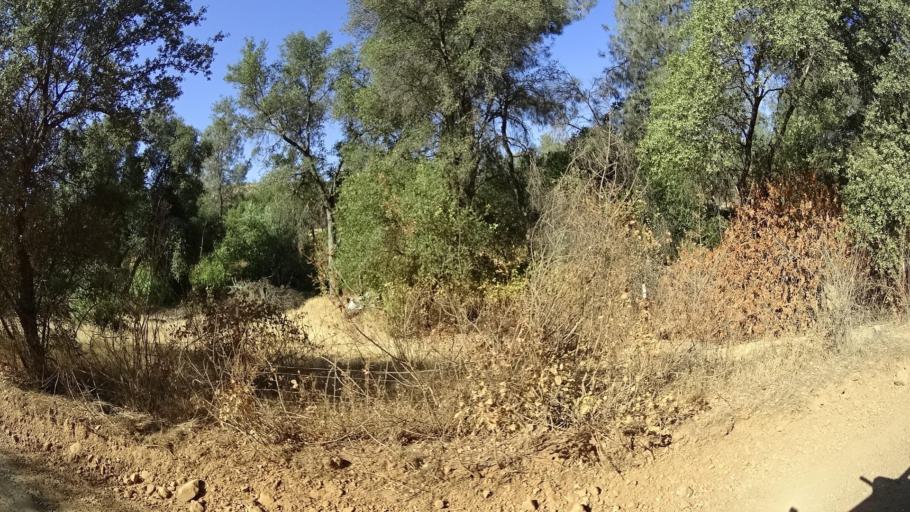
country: US
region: California
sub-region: Mariposa County
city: Mariposa
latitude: 37.6182
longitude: -120.2142
